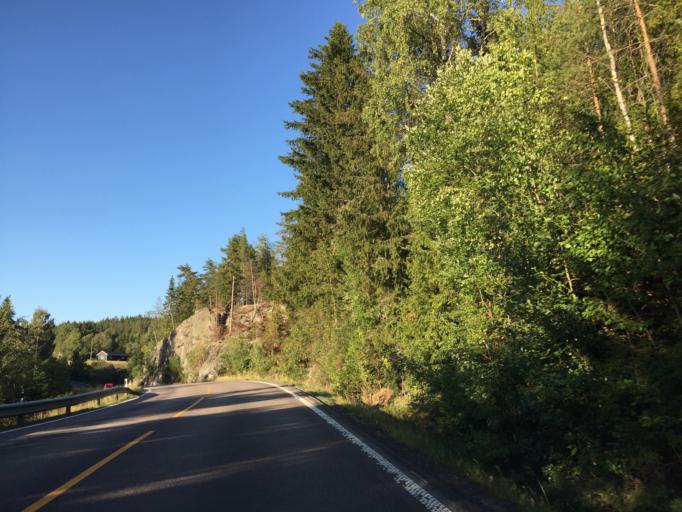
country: NO
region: Akershus
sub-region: Enebakk
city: Kirkebygda
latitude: 59.7769
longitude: 11.2770
